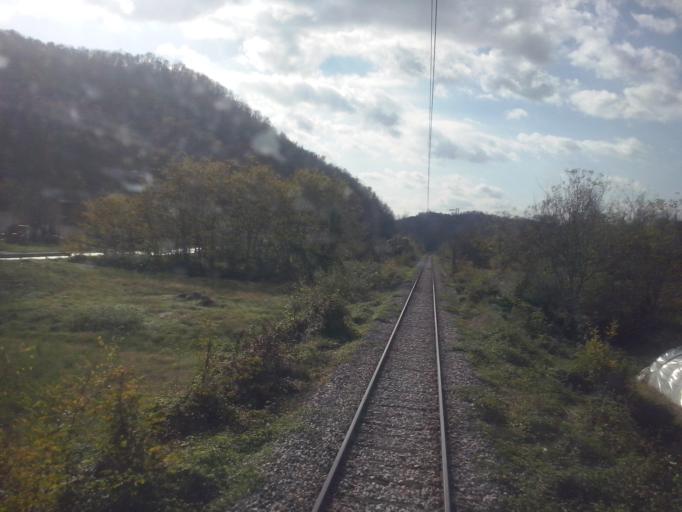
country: RS
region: Central Serbia
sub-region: Zlatiborski Okrug
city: Pozega
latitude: 43.9003
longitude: 19.9991
